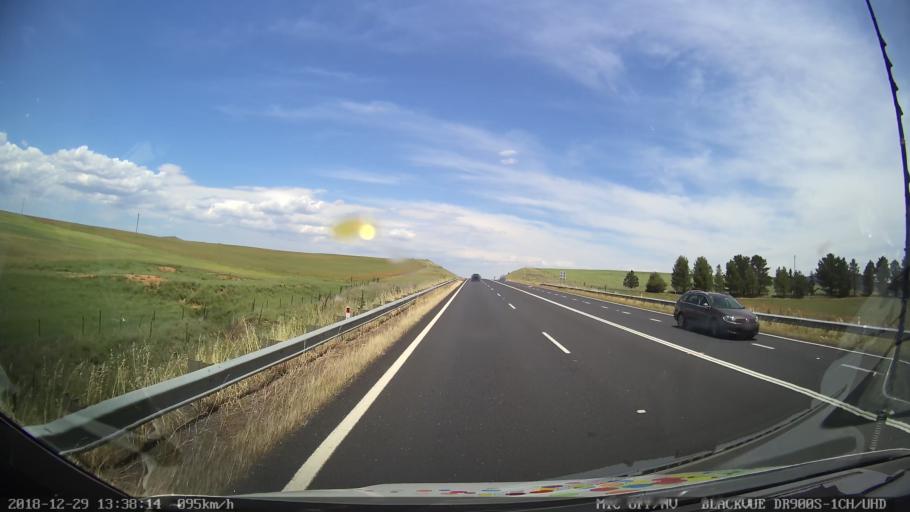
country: AU
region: New South Wales
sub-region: Cooma-Monaro
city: Cooma
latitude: -35.9957
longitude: 149.1405
